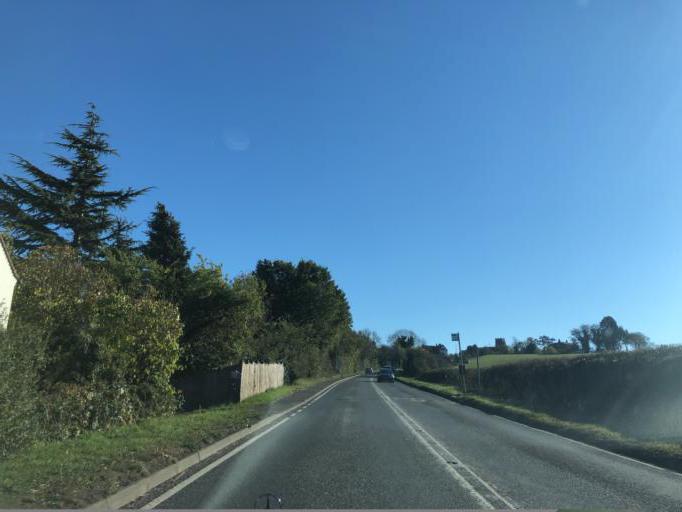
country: GB
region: England
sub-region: Warwickshire
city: Harbury
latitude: 52.2597
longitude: -1.4500
